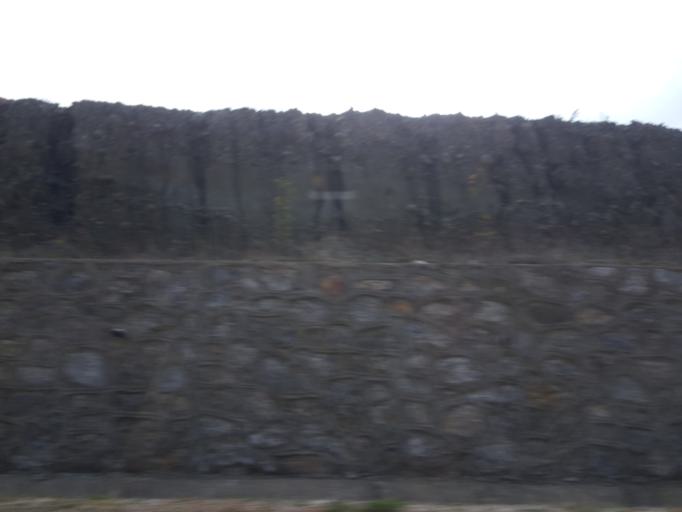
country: TR
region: Sinop
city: Sarayduzu
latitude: 41.3880
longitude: 34.9411
